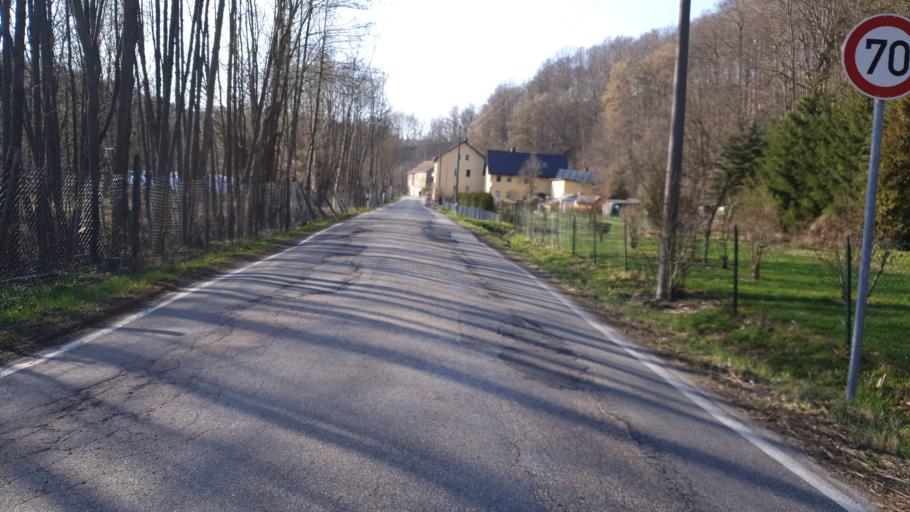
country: DE
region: Saxony
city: Burgstadt
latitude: 50.9446
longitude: 12.8174
